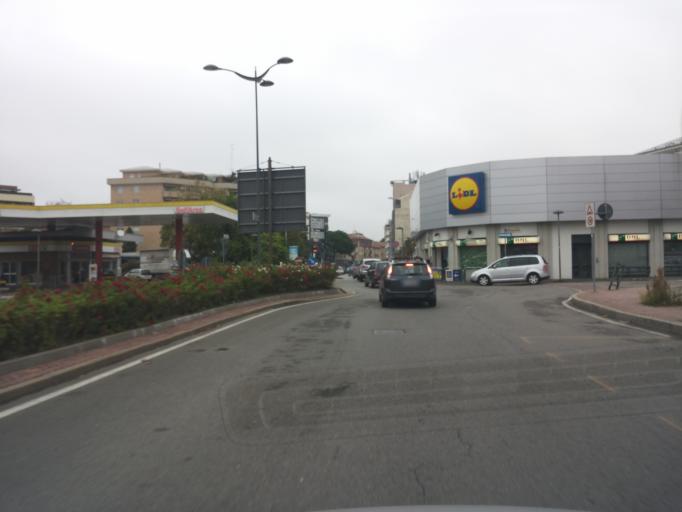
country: IT
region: Piedmont
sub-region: Provincia di Novara
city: Torrion Quartara
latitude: 45.4369
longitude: 8.6052
